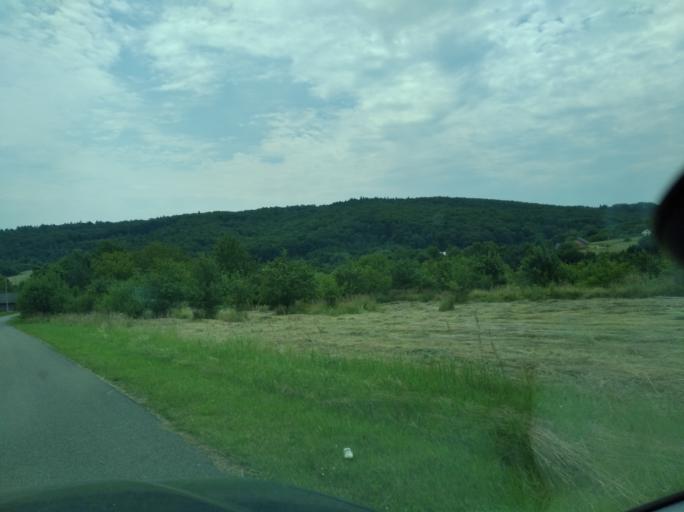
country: PL
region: Subcarpathian Voivodeship
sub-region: Powiat przeworski
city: Lopuszka Wielka
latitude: 49.9001
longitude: 22.4192
